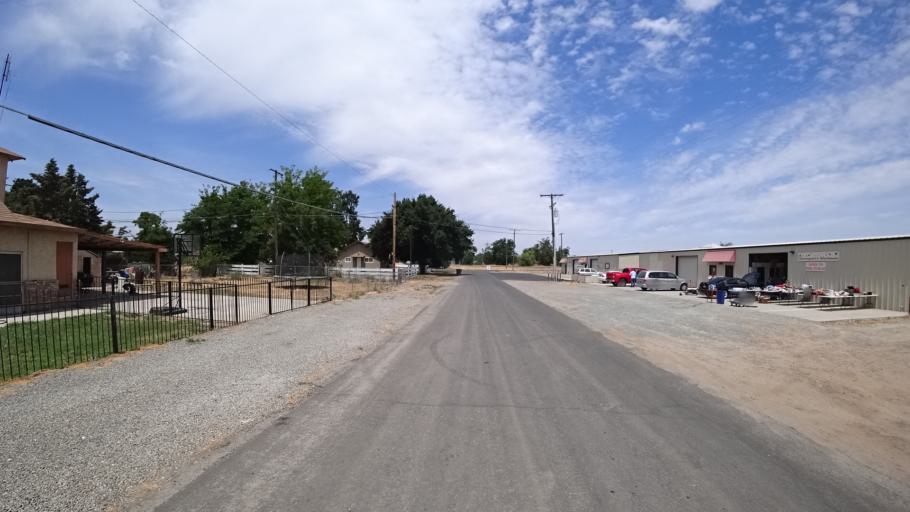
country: US
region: California
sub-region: Kings County
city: Armona
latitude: 36.3144
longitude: -119.7057
